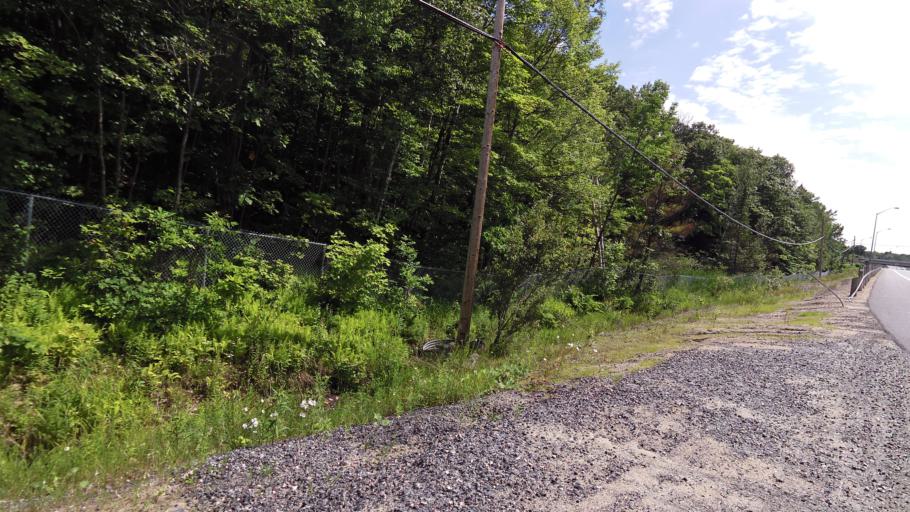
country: CA
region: Ontario
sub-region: Parry Sound District
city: Parry Sound
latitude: 45.3856
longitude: -80.0381
